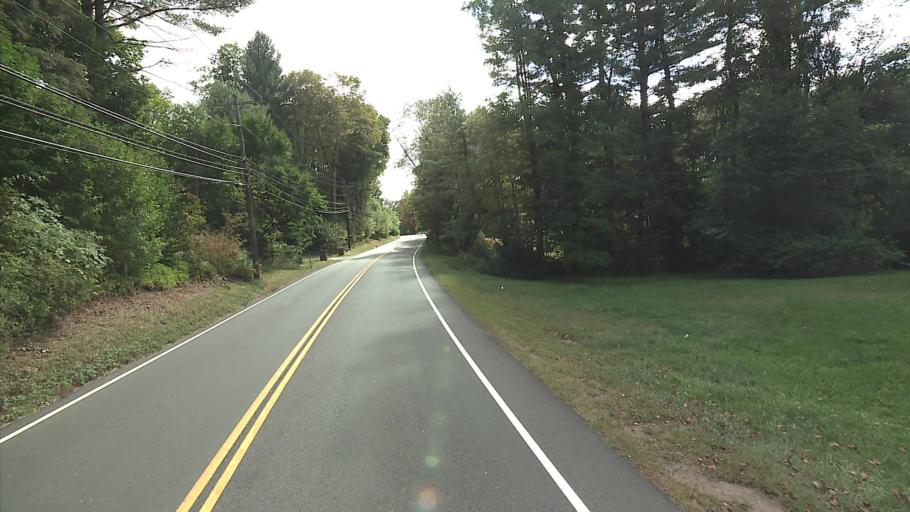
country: US
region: Connecticut
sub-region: Middlesex County
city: Durham
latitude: 41.4883
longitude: -72.6882
